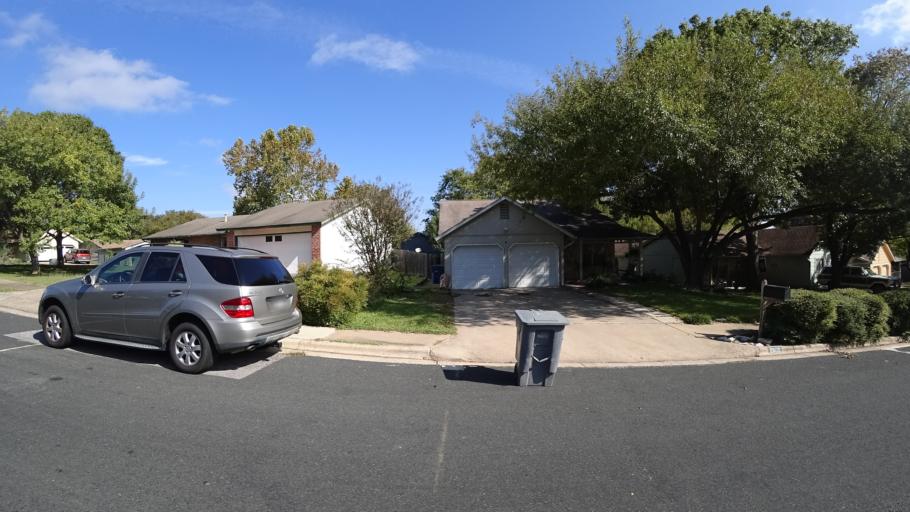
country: US
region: Texas
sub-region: Travis County
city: Shady Hollow
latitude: 30.1915
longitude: -97.8230
